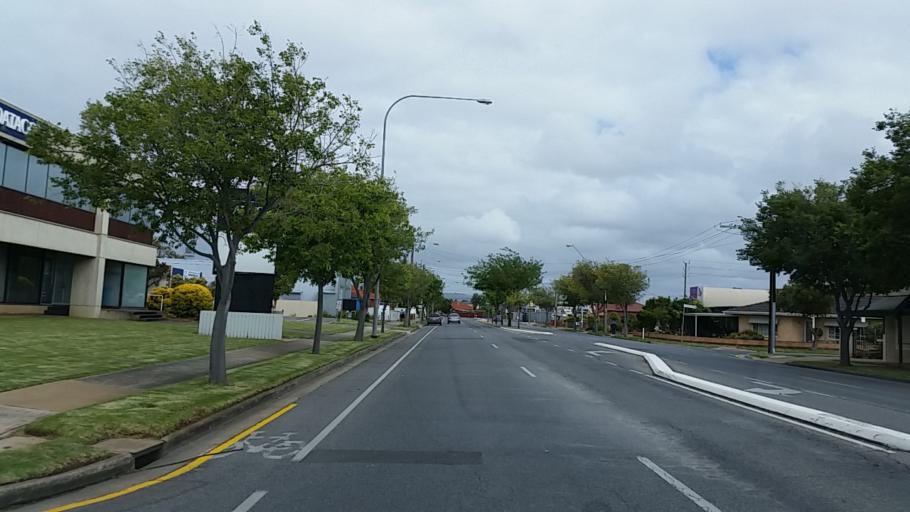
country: AU
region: South Australia
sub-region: Charles Sturt
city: Findon
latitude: -34.9033
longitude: 138.5441
